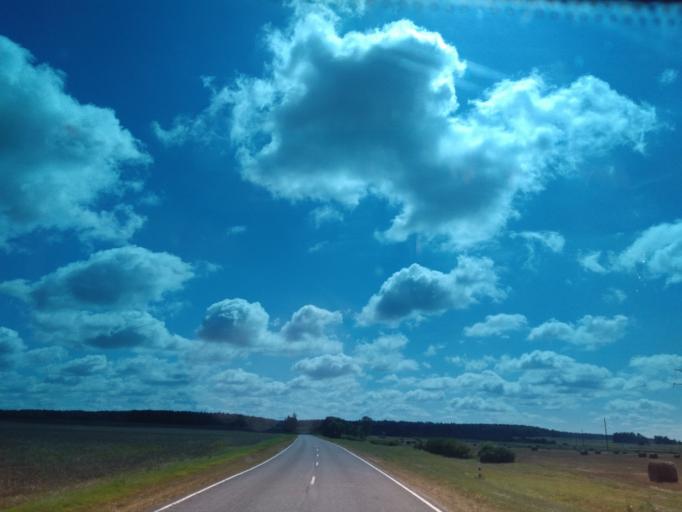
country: BY
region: Minsk
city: Uzda
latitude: 53.3944
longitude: 27.2344
